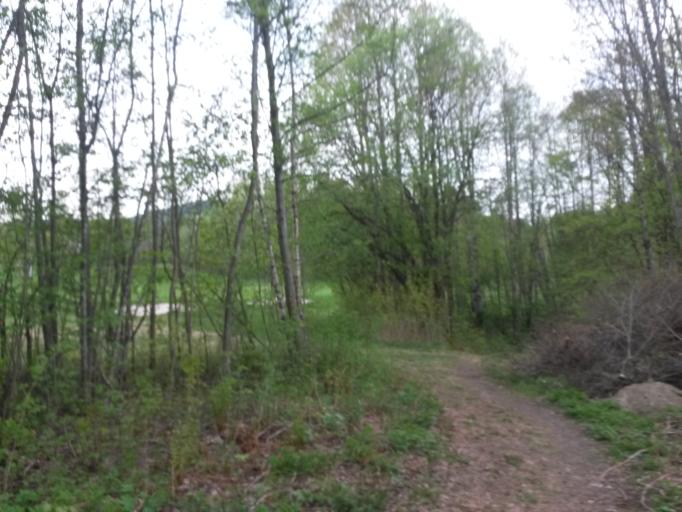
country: NO
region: Akershus
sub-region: Asker
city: Asker
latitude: 59.8349
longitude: 10.4058
